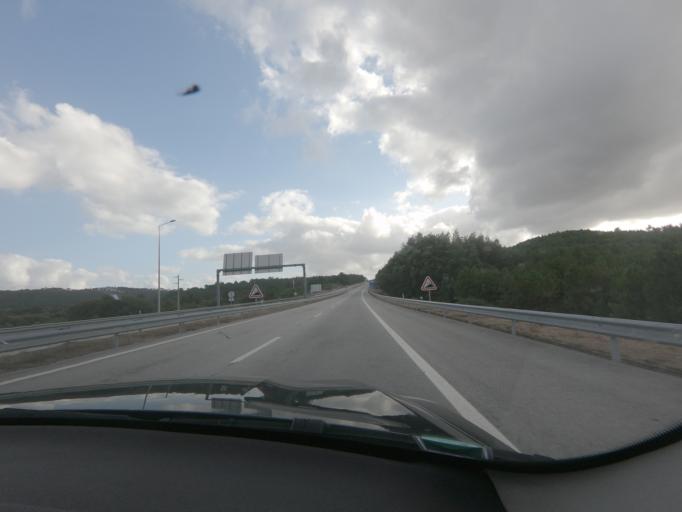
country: PT
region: Viseu
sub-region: Viseu
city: Campo
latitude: 40.7041
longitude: -7.9497
